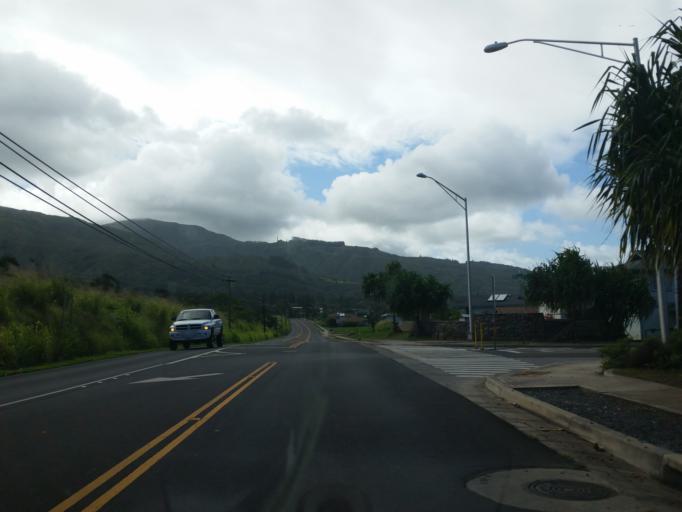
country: US
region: Hawaii
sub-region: Maui County
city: Waihee-Waiehu
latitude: 20.9257
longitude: -156.5051
